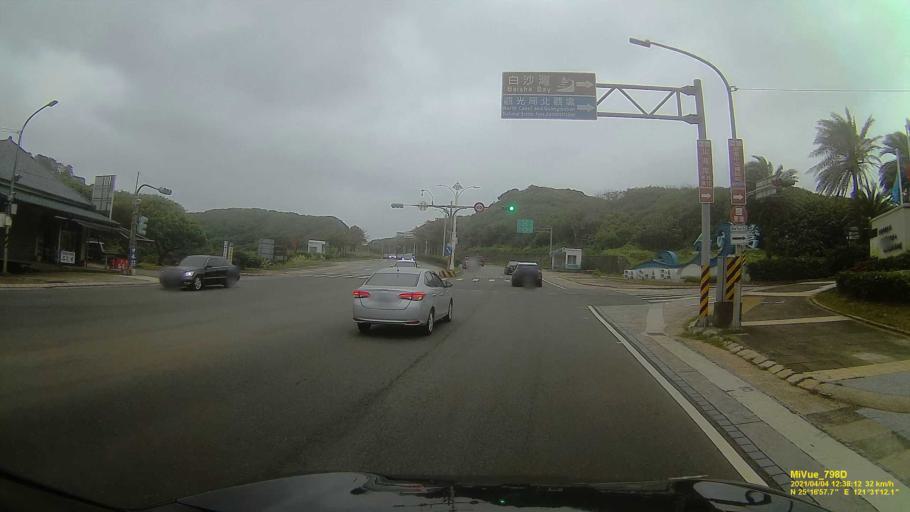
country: TW
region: Taipei
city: Taipei
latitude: 25.2826
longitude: 121.5200
